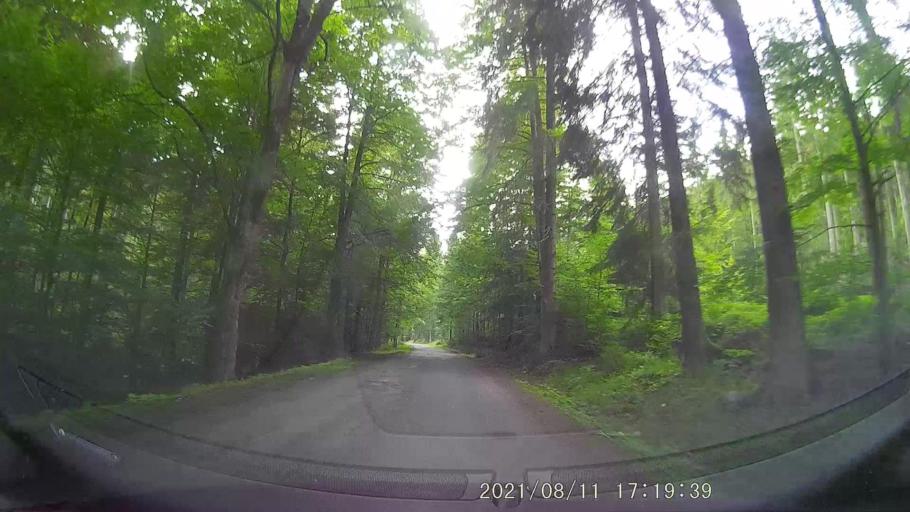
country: PL
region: Lower Silesian Voivodeship
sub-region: Powiat klodzki
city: Polanica-Zdroj
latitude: 50.3055
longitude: 16.5191
